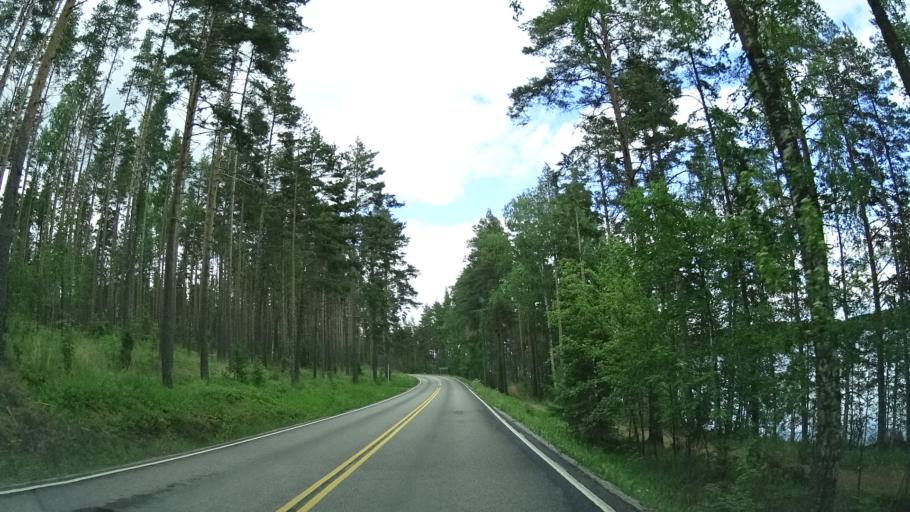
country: FI
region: Paijanne Tavastia
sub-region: Lahti
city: Asikkala
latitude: 61.3075
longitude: 25.5463
